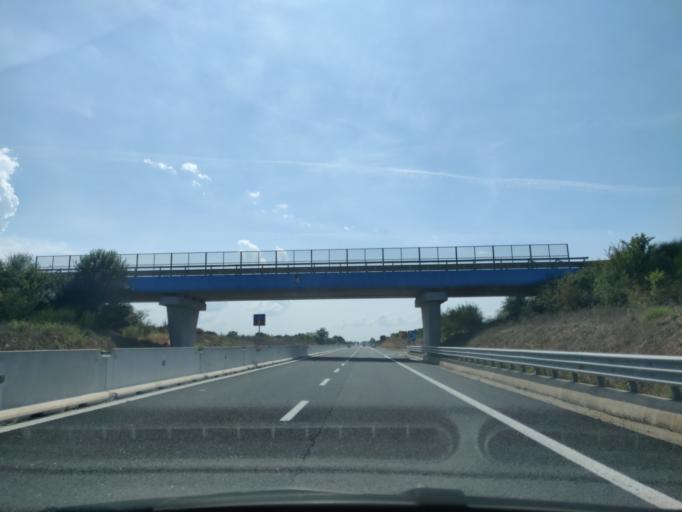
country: IT
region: Latium
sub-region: Provincia di Viterbo
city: Blera
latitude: 42.3409
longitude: 11.9828
